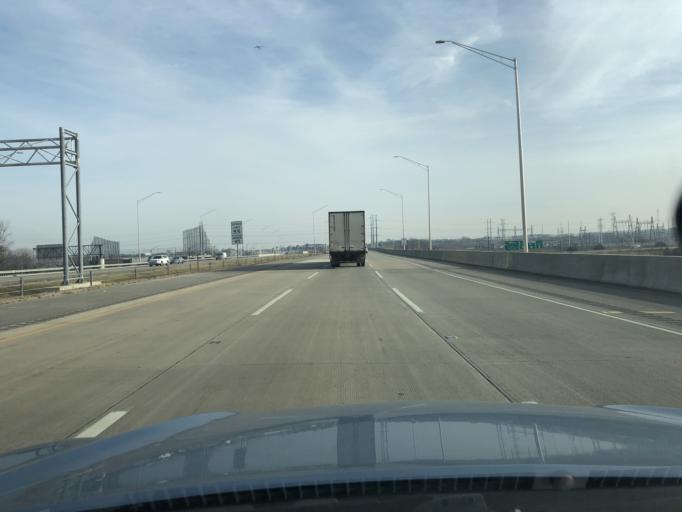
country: US
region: Illinois
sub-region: DuPage County
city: Itasca
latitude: 41.9837
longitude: -88.0026
